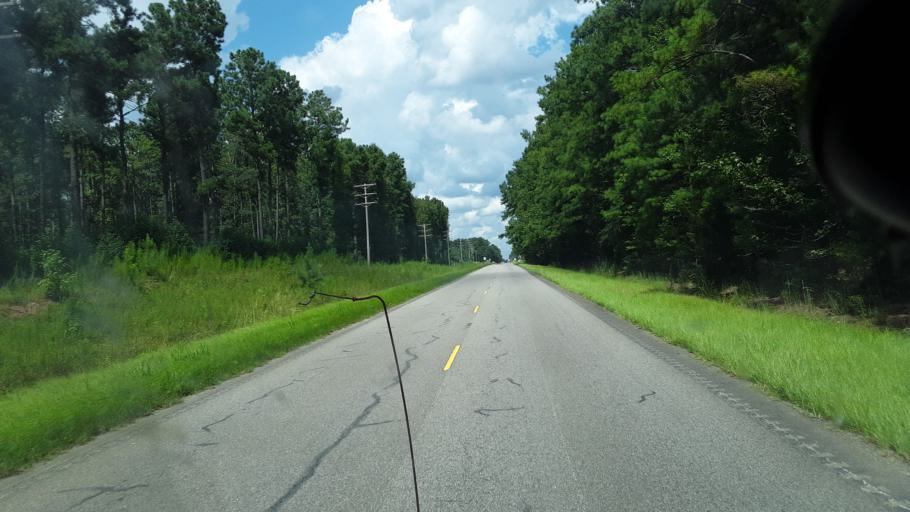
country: US
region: South Carolina
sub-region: Williamsburg County
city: Andrews
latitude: 33.5905
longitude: -79.4444
